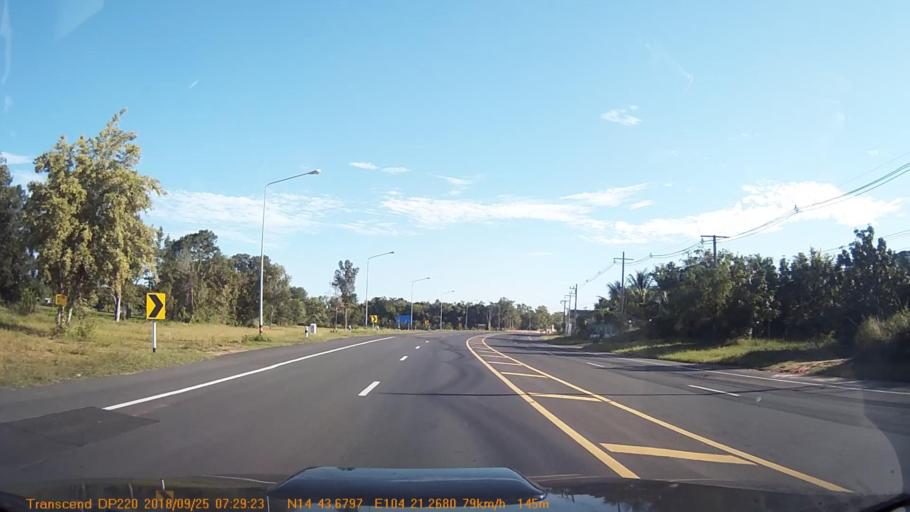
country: TH
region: Sisaket
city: Phrai Bueng
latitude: 14.7285
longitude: 104.3545
